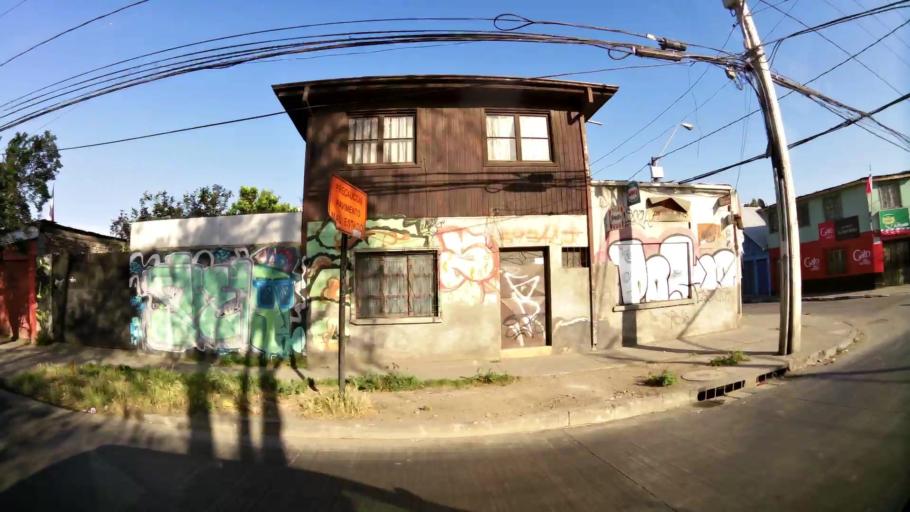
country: CL
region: Santiago Metropolitan
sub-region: Provincia de Santiago
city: Santiago
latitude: -33.3734
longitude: -70.6713
